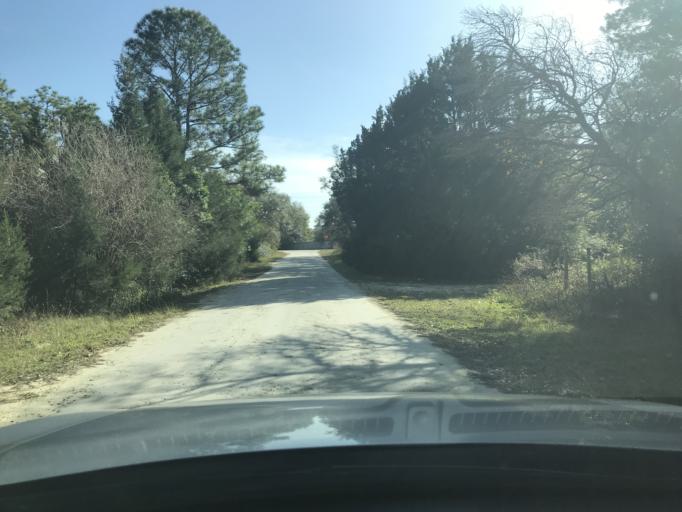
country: US
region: Florida
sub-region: Hernando County
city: North Weeki Wachee
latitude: 28.5492
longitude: -82.5702
